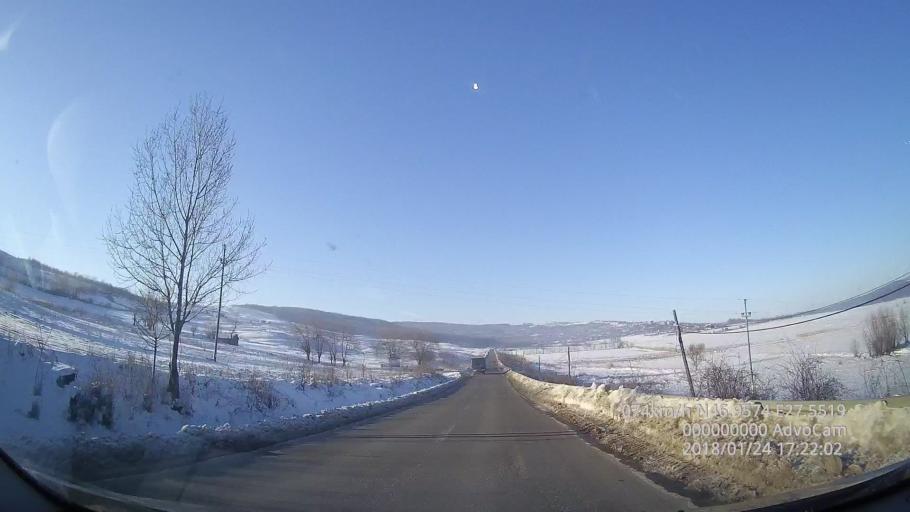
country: RO
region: Iasi
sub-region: Comuna Grajduri
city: Grajduri
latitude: 46.9578
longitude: 27.5513
